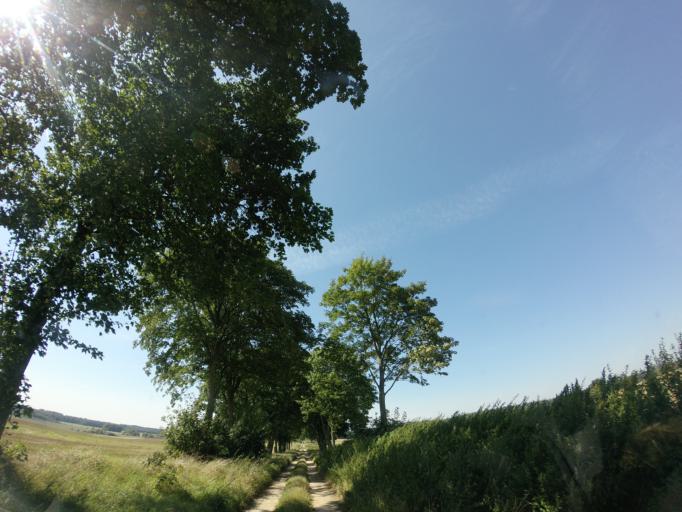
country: PL
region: West Pomeranian Voivodeship
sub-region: Powiat choszczenski
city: Choszczno
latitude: 53.1786
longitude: 15.3798
